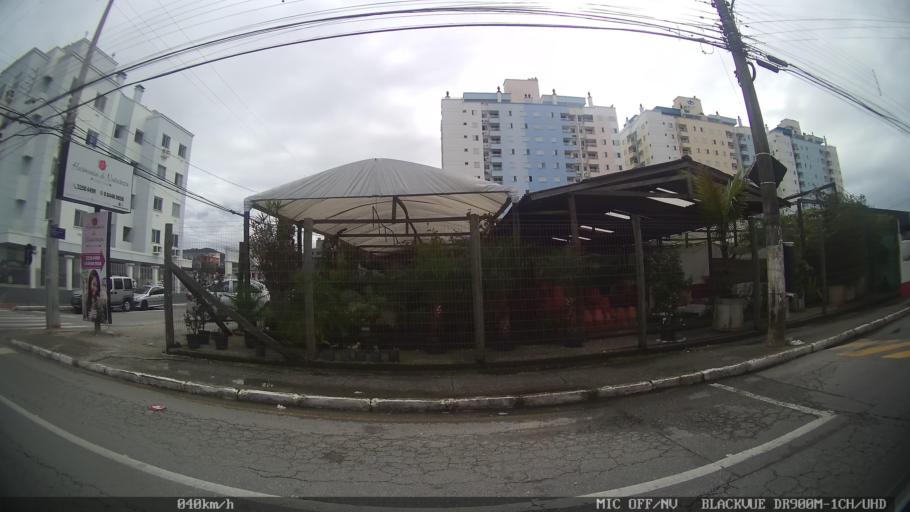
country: BR
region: Santa Catarina
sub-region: Sao Jose
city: Campinas
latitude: -27.5591
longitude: -48.6307
